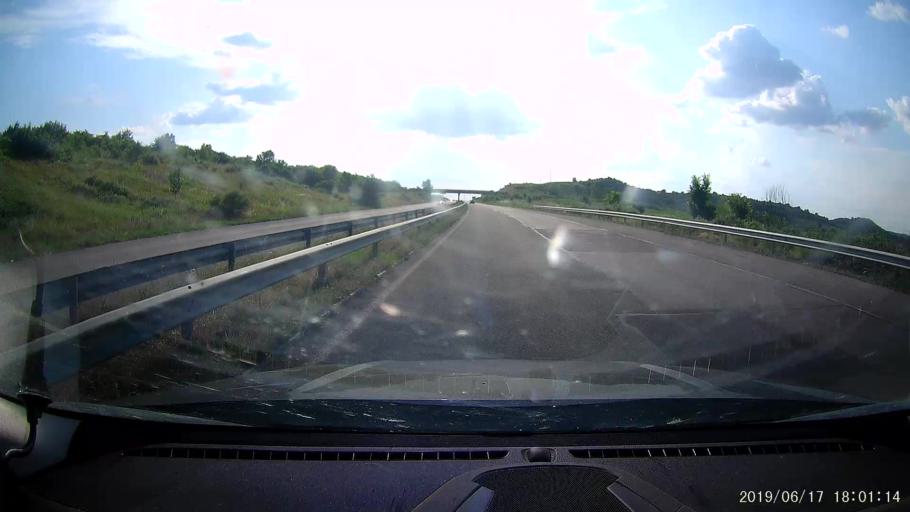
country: BG
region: Khaskovo
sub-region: Obshtina Svilengrad
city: Svilengrad
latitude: 41.7450
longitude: 26.2606
